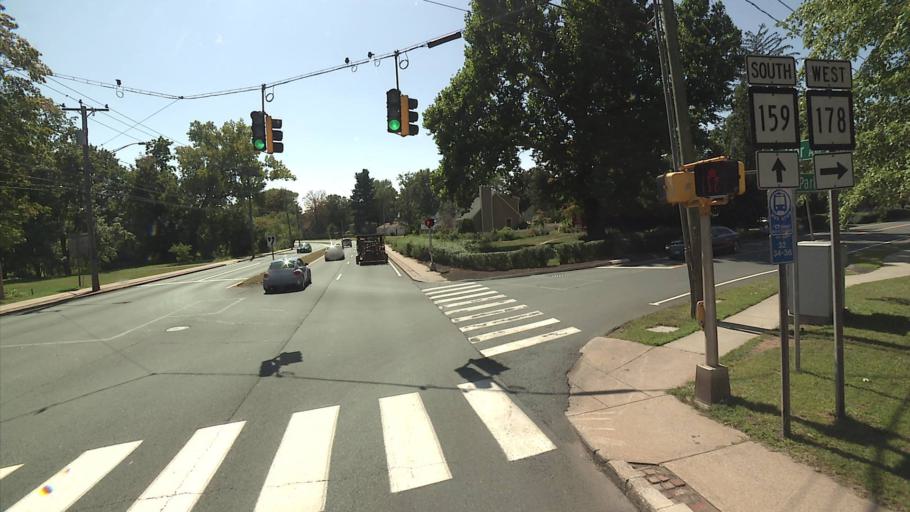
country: US
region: Connecticut
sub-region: Hartford County
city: Windsor
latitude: 41.8389
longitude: -72.6521
